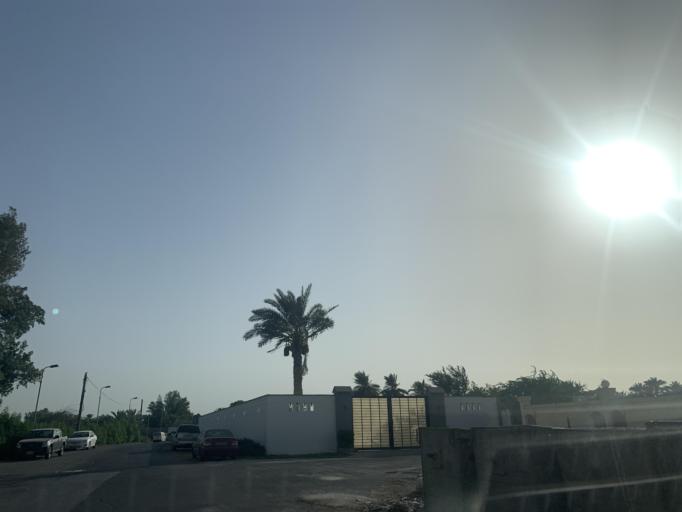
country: BH
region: Northern
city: Madinat `Isa
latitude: 26.1901
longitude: 50.4633
